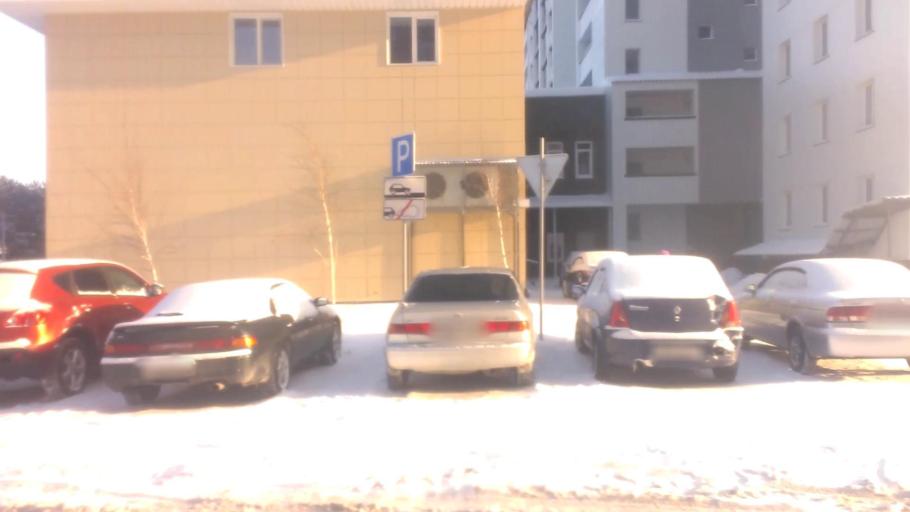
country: RU
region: Altai Krai
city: Novosilikatnyy
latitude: 53.3454
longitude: 83.6557
